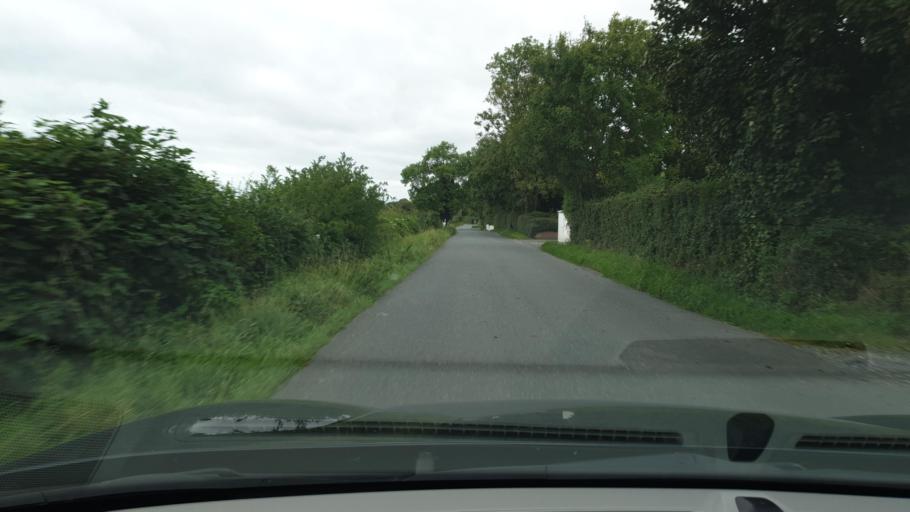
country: IE
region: Leinster
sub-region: Kildare
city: Kilcock
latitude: 53.3978
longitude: -6.6364
